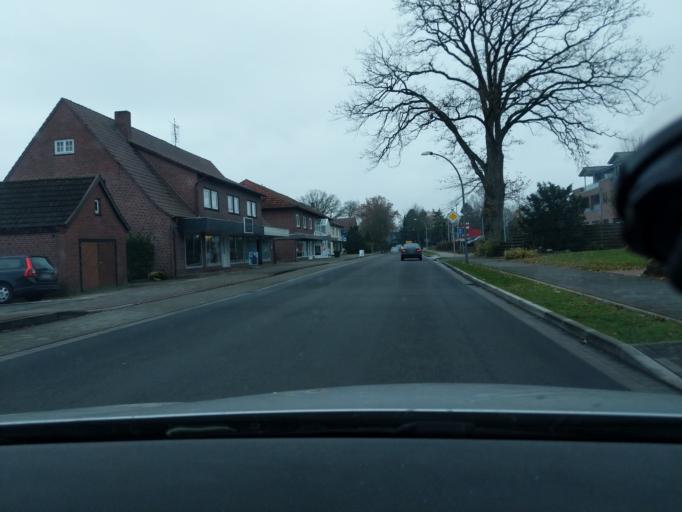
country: DE
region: Lower Saxony
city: Heeslingen
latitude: 53.3183
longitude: 9.3384
